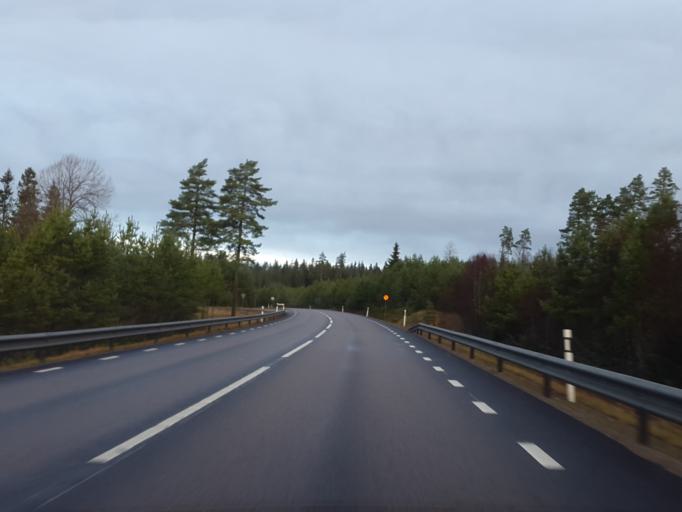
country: SE
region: Vaestra Goetaland
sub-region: Boras Kommun
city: Sandared
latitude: 57.7915
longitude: 12.7701
